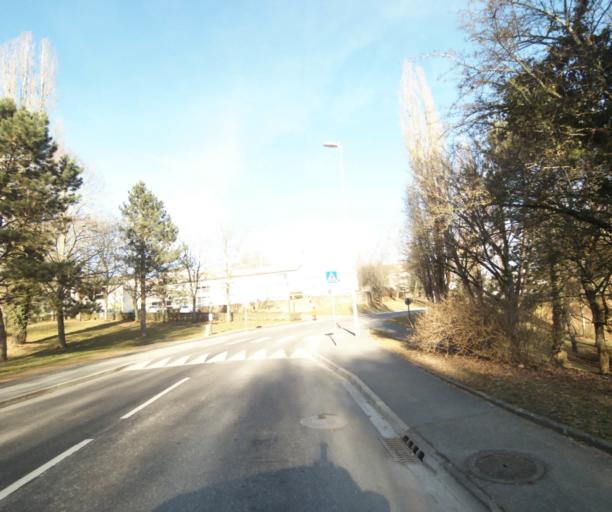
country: FR
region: Lorraine
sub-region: Departement de Meurthe-et-Moselle
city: Chavigny
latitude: 48.6573
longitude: 6.1154
